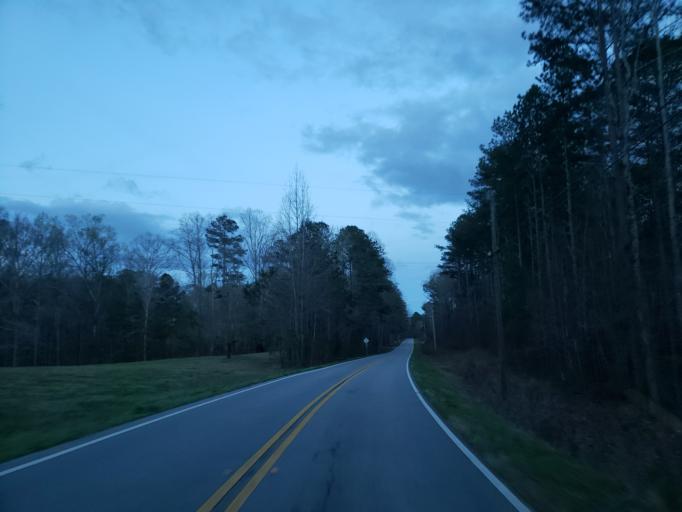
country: US
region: Georgia
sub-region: Paulding County
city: Dallas
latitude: 34.0073
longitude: -84.9092
